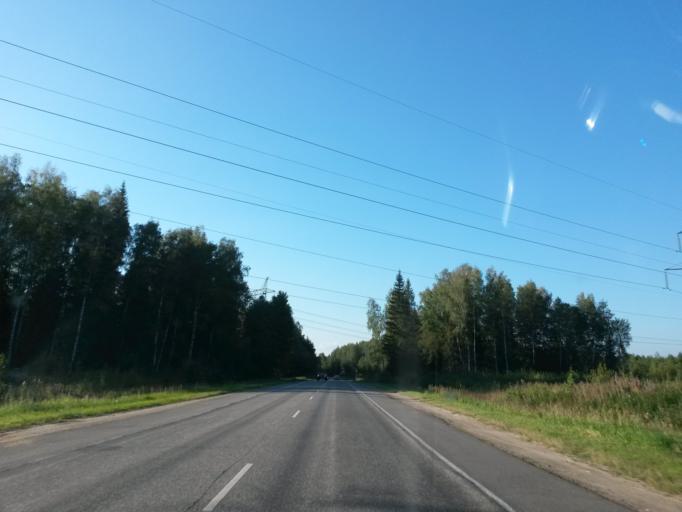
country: RU
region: Ivanovo
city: Pistsovo
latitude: 57.1058
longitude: 40.6519
